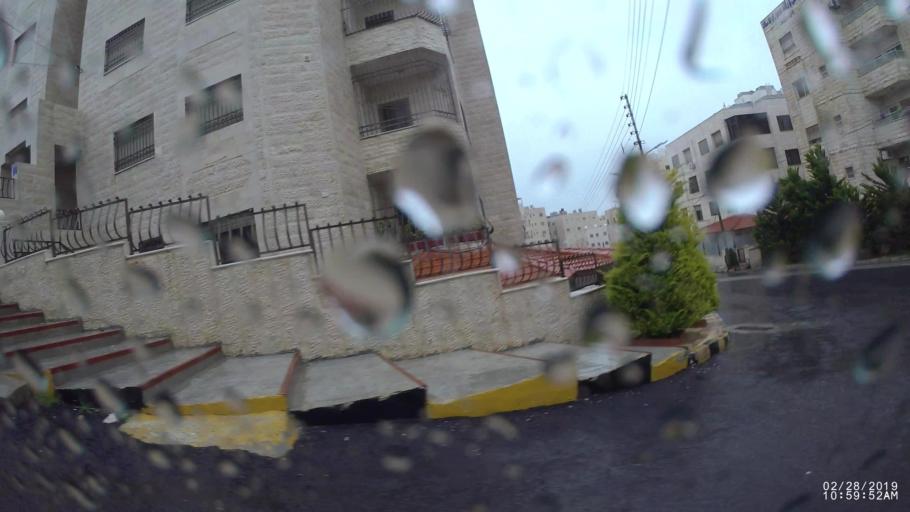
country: JO
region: Amman
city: Al Jubayhah
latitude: 32.0150
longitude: 35.8915
